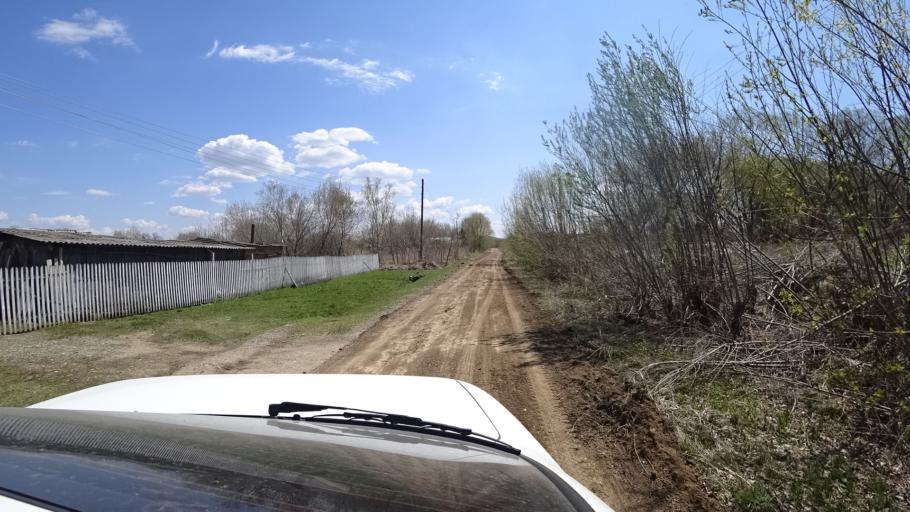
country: RU
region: Primorskiy
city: Lazo
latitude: 45.8001
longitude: 133.7605
